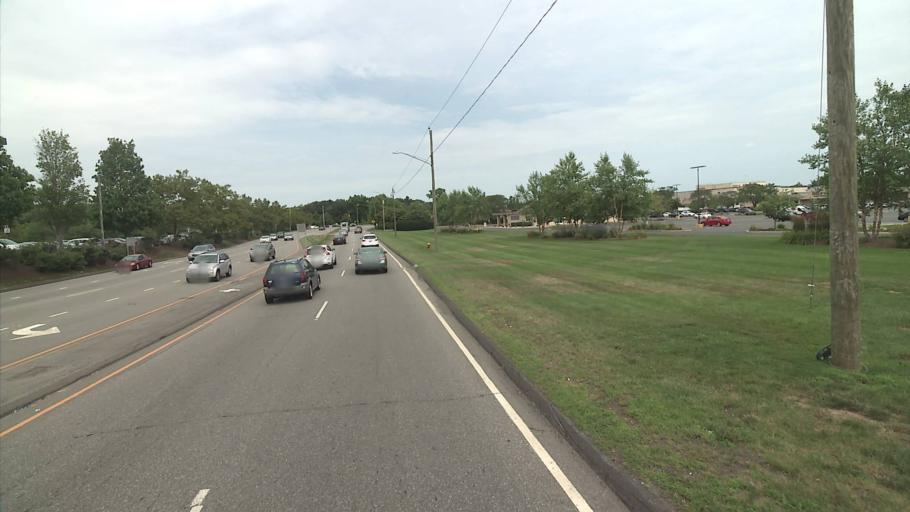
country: US
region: Connecticut
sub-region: Hartford County
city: West Hartford
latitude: 41.7240
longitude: -72.7601
